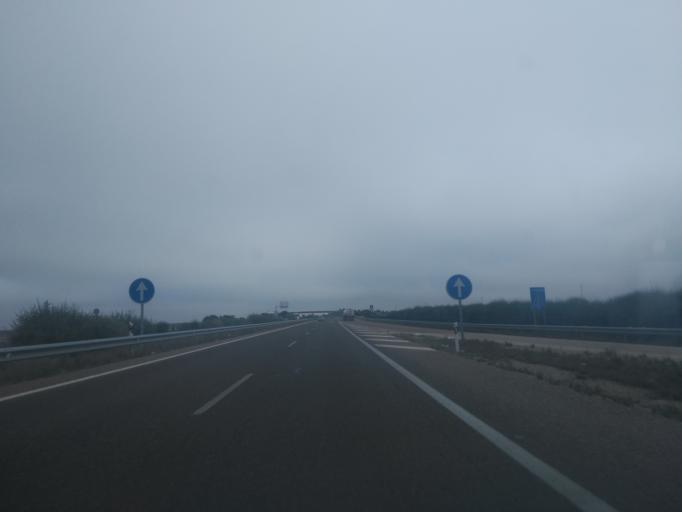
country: ES
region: Castille and Leon
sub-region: Provincia de Salamanca
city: Castellanos de Moriscos
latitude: 41.0297
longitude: -5.5718
